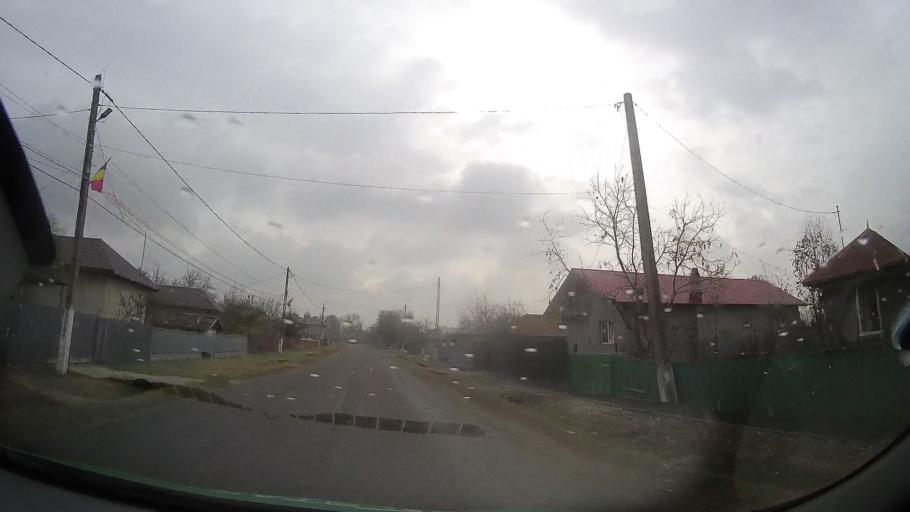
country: RO
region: Prahova
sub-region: Comuna Draganesti
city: Draganesti
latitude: 44.8428
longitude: 26.2689
